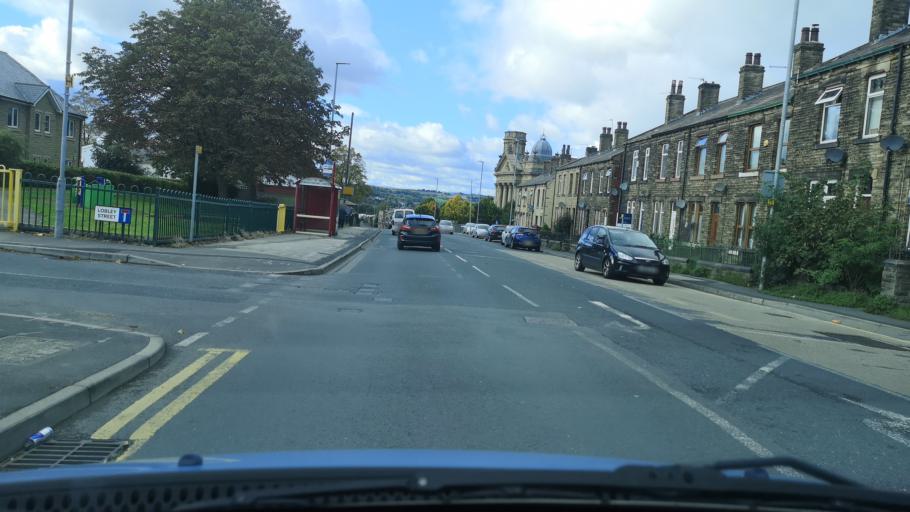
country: GB
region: England
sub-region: Kirklees
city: Heckmondwike
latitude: 53.7092
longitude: -1.6622
